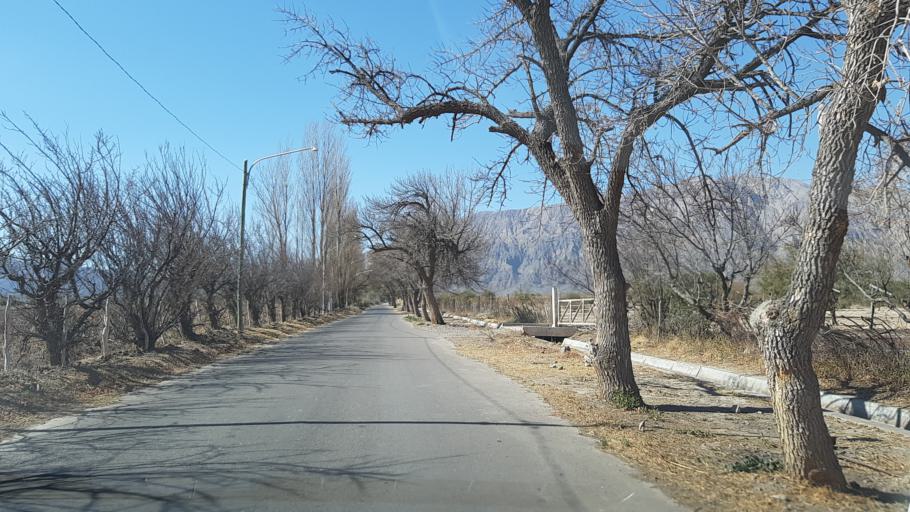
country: AR
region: San Juan
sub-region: Departamento de Zonda
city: Zonda
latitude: -31.5714
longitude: -68.7538
